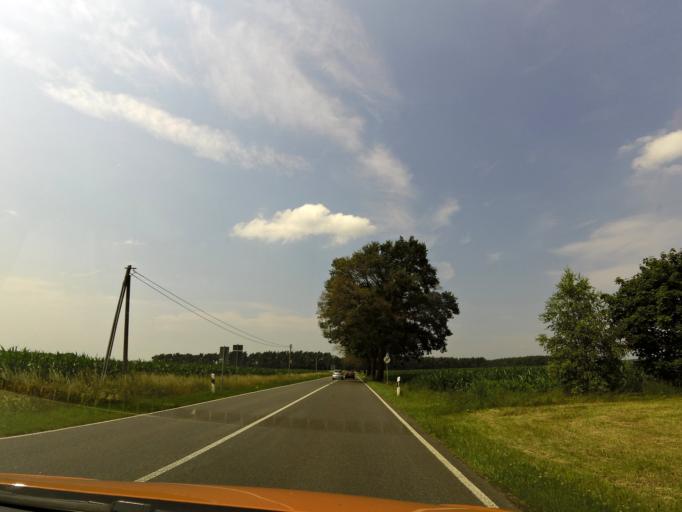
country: DE
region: Brandenburg
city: Gumtow
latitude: 53.0301
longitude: 12.2817
